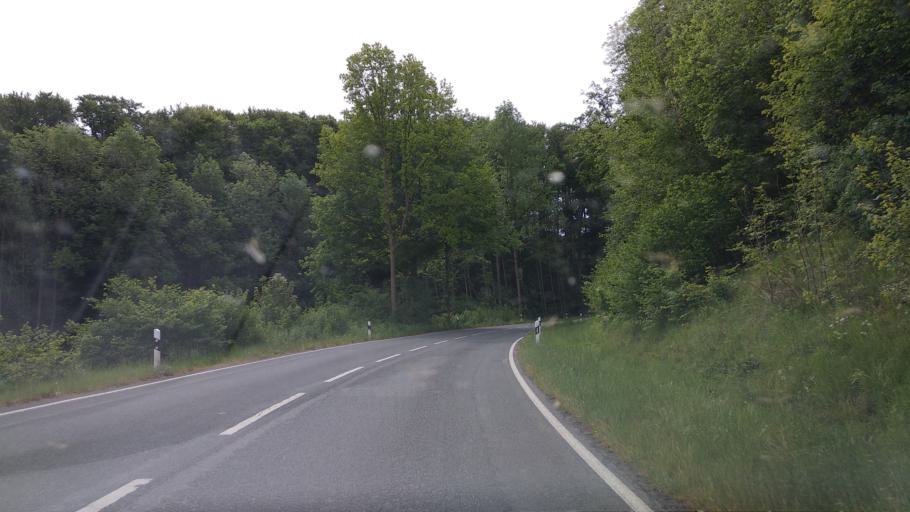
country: DE
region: North Rhine-Westphalia
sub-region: Regierungsbezirk Detmold
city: Willebadessen
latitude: 51.6223
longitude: 9.1008
